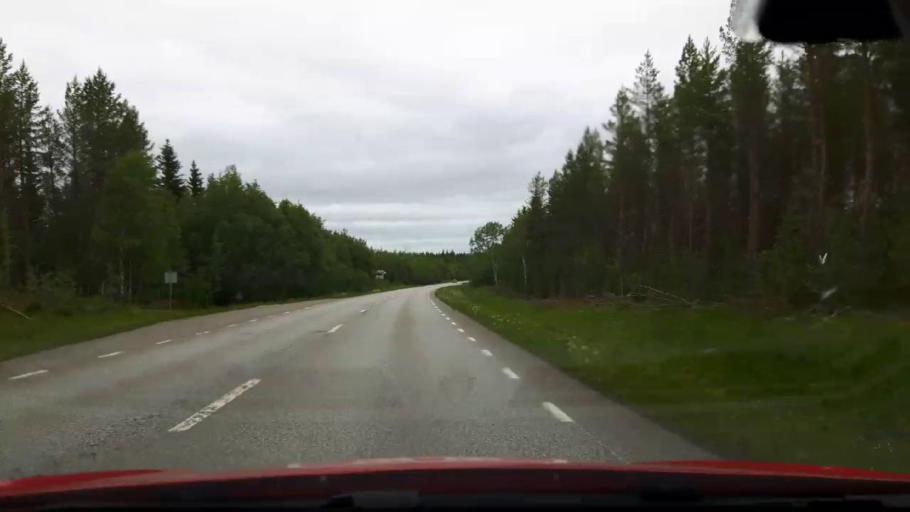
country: SE
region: Jaemtland
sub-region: OEstersunds Kommun
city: Lit
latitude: 63.5913
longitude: 14.6415
